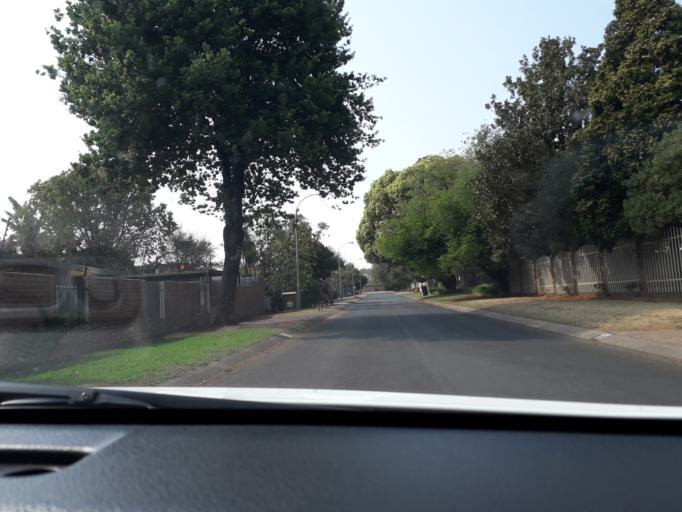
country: ZA
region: Gauteng
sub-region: City of Johannesburg Metropolitan Municipality
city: Modderfontein
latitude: -26.0800
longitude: 28.2405
